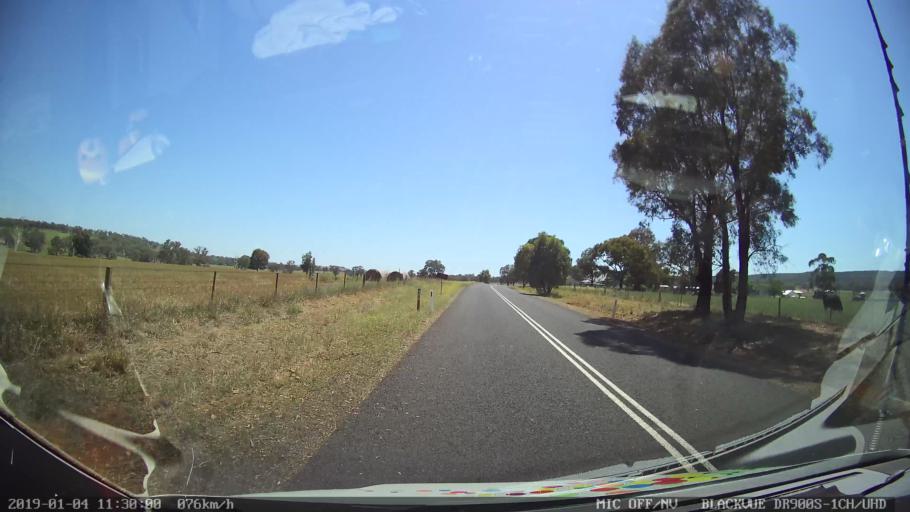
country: AU
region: New South Wales
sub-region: Cabonne
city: Molong
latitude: -33.0814
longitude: 148.7768
